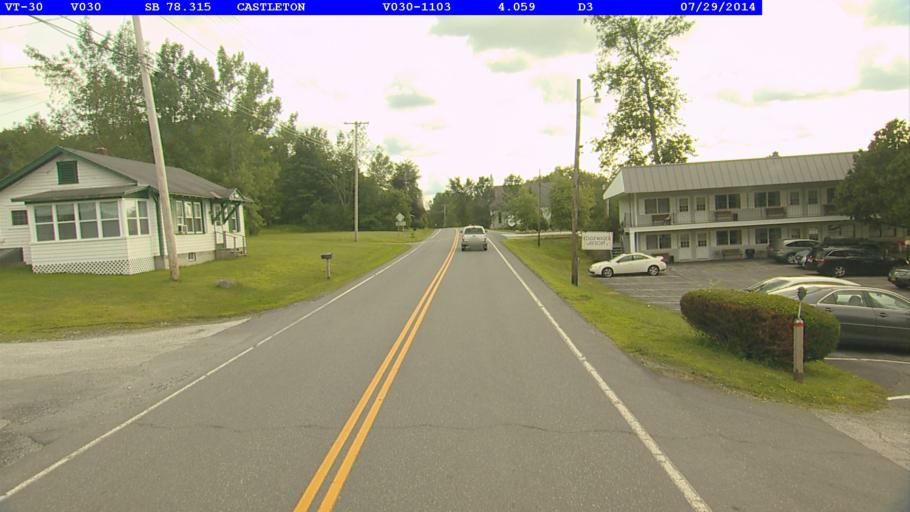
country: US
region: Vermont
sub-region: Rutland County
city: Castleton
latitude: 43.6445
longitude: -73.1984
